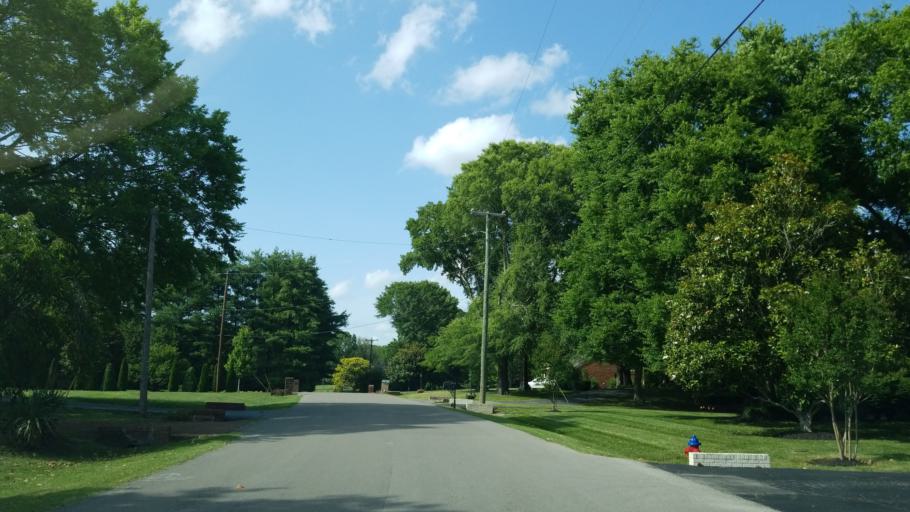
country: US
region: Tennessee
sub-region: Davidson County
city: Forest Hills
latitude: 36.0331
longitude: -86.8245
